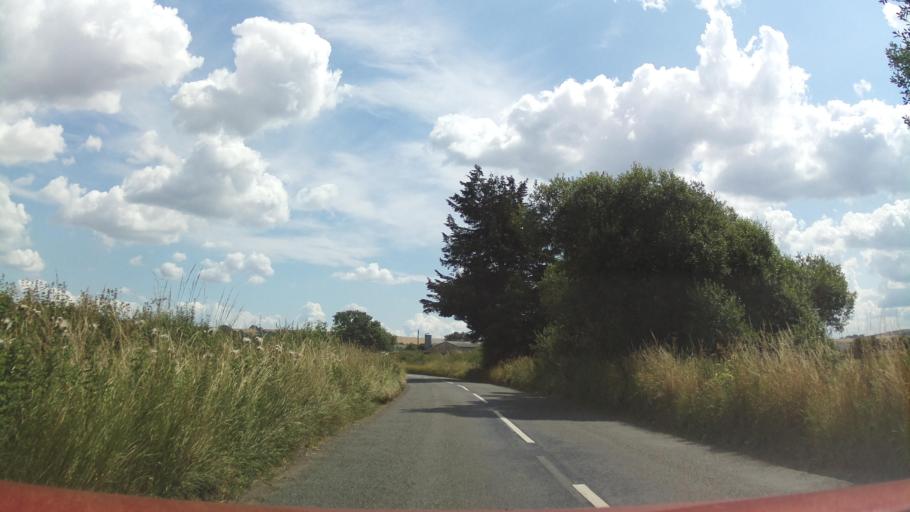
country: GB
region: England
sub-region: Borough of Swindon
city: Bishopstone
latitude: 51.5749
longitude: -1.6370
